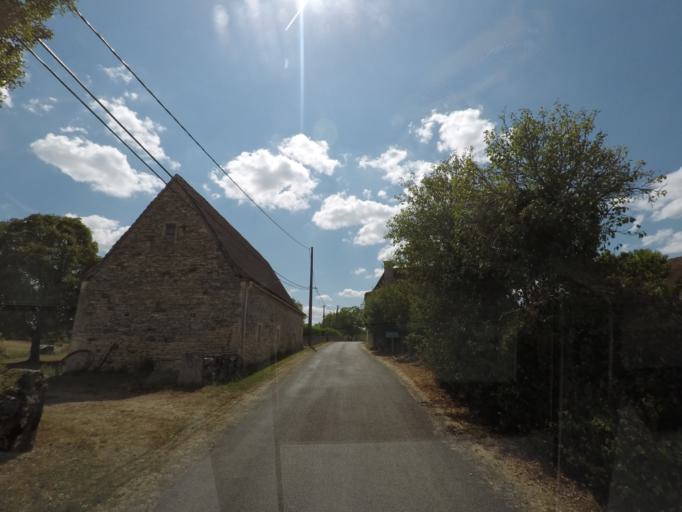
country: FR
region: Midi-Pyrenees
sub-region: Departement du Lot
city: Cajarc
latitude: 44.5475
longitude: 1.6693
